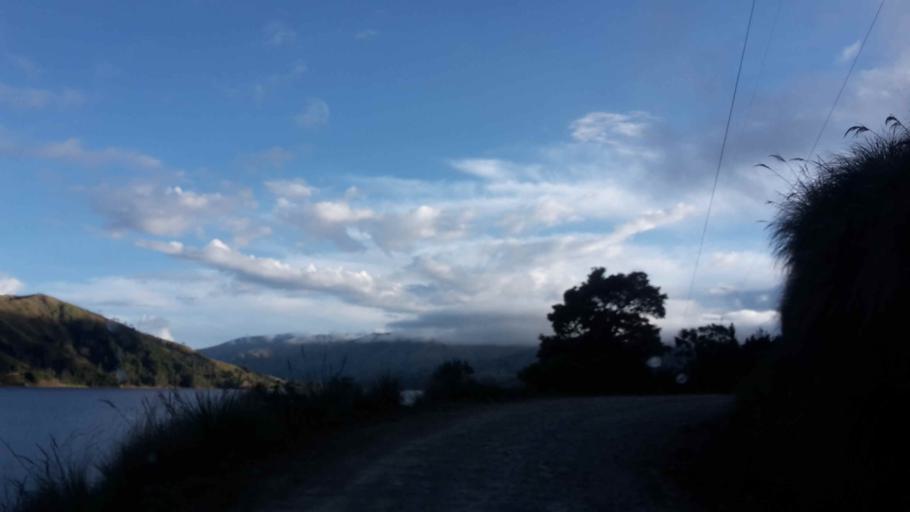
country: BO
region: Cochabamba
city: Colomi
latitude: -17.2579
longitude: -65.9050
